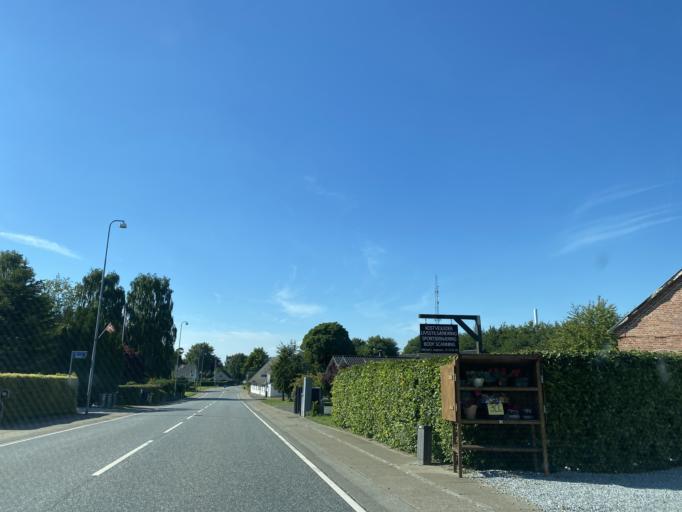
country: DK
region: Central Jutland
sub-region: Hedensted Kommune
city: Torring
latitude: 55.8572
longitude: 9.4258
